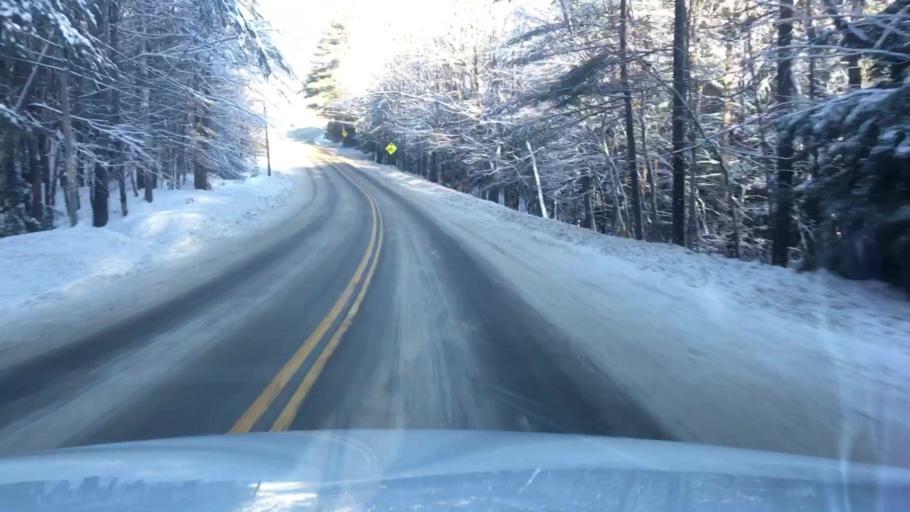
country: US
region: Maine
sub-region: Kennebec County
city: Readfield
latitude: 44.4323
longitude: -69.9645
